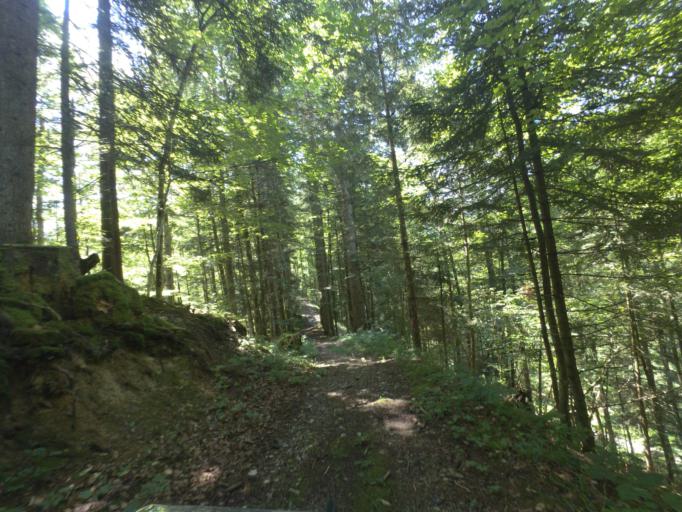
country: AT
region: Salzburg
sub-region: Politischer Bezirk Salzburg-Umgebung
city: Hintersee
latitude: 47.7063
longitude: 13.2838
